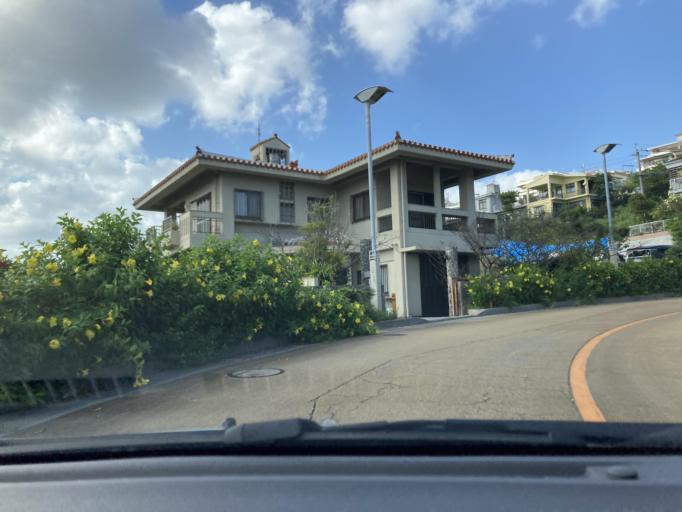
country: JP
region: Okinawa
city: Naha-shi
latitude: 26.2164
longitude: 127.7109
